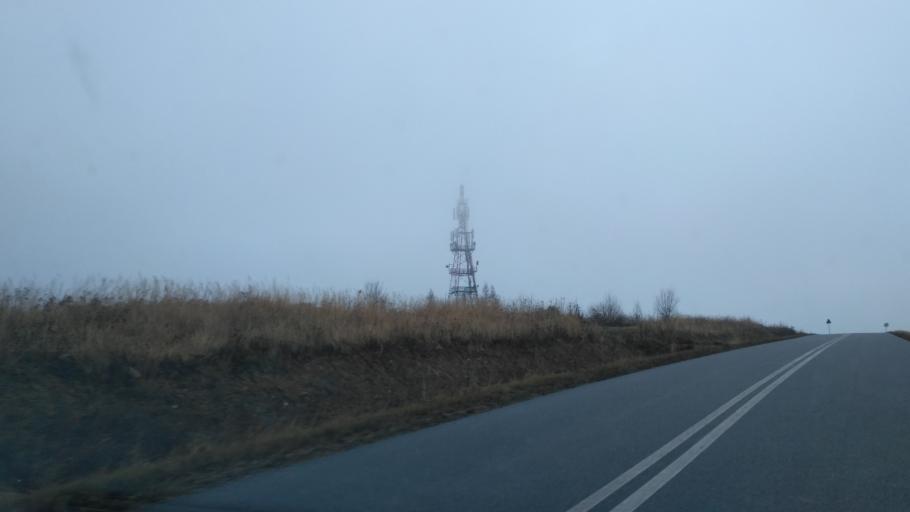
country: PL
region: Subcarpathian Voivodeship
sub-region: Powiat jaroslawski
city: Jodlowka
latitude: 49.8994
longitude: 22.4847
